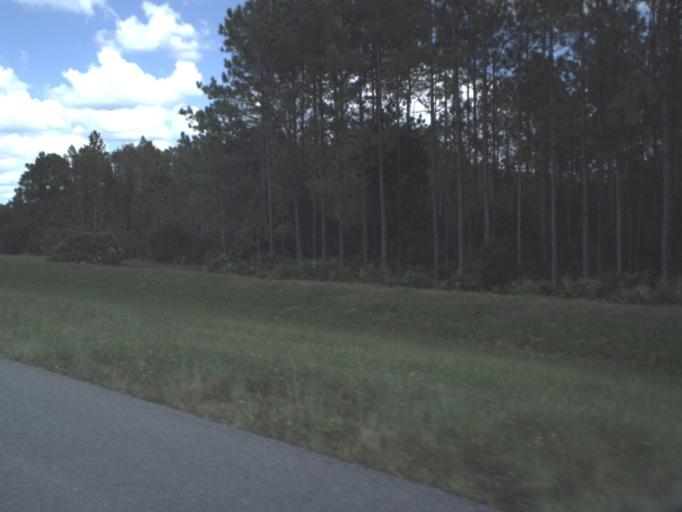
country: US
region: Florida
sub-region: Pasco County
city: Odessa
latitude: 28.2763
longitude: -82.5502
